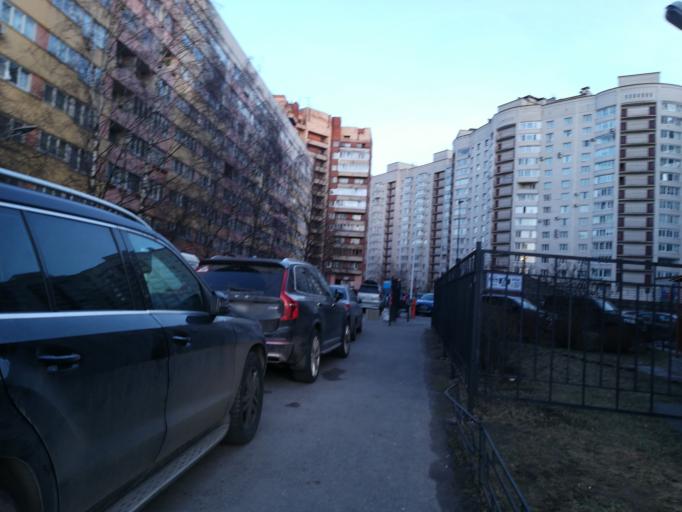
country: RU
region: St.-Petersburg
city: Dachnoye
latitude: 59.8536
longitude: 30.2251
